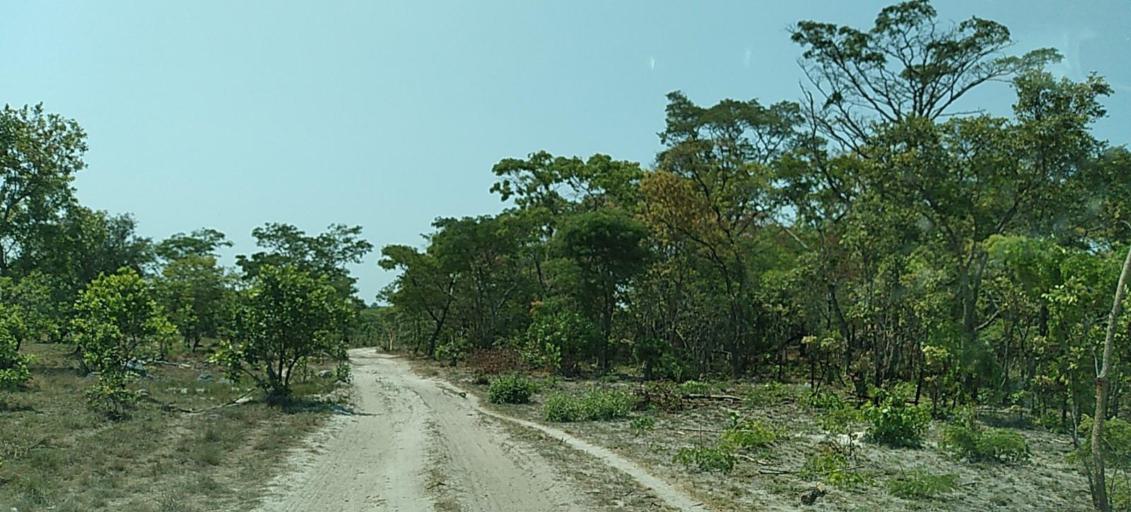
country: ZM
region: Copperbelt
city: Mpongwe
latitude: -13.8490
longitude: 28.0571
